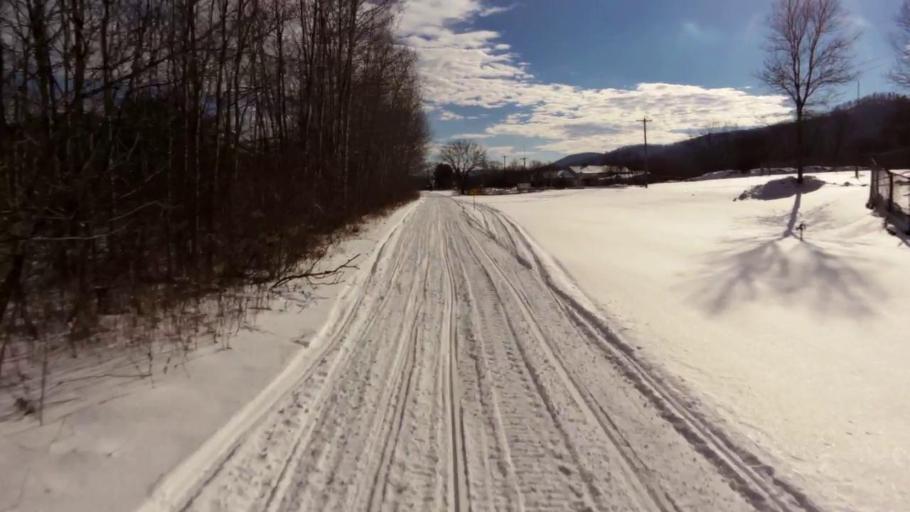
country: US
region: Pennsylvania
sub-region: McKean County
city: Foster Brook
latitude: 42.0273
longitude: -78.6316
